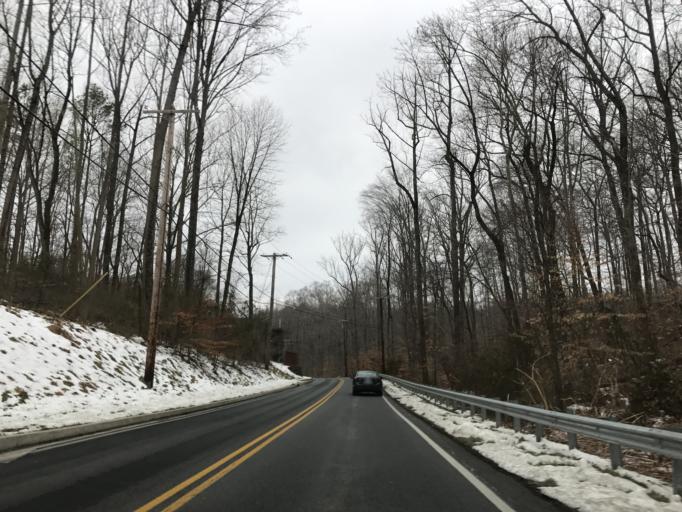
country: US
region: Maryland
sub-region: Harford County
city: Bel Air South
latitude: 39.5050
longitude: -76.3037
